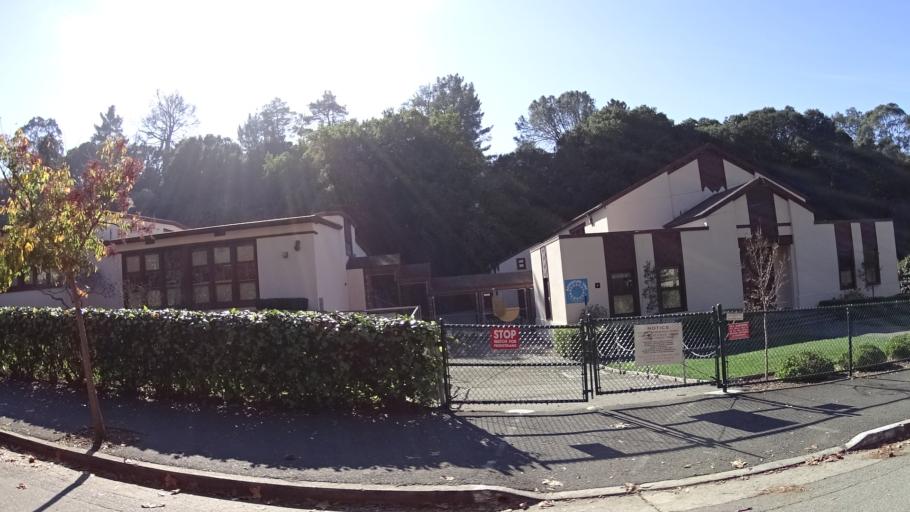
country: US
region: California
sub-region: Alameda County
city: Piedmont
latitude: 37.8314
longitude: -122.2131
